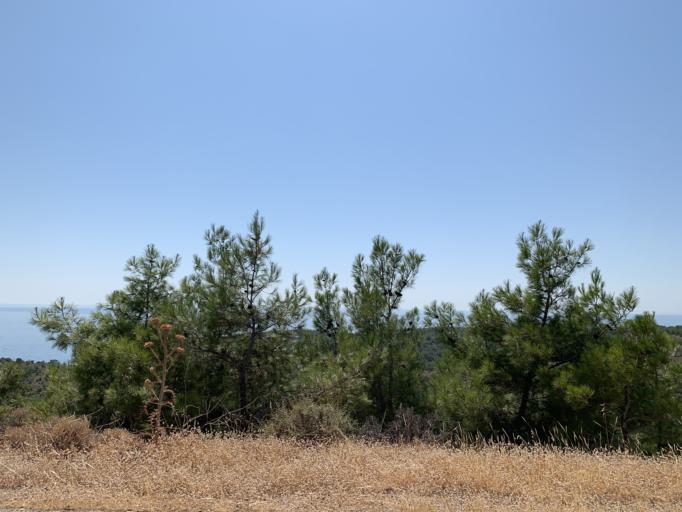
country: GR
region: North Aegean
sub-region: Chios
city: Vrontados
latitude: 38.4070
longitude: 25.9737
